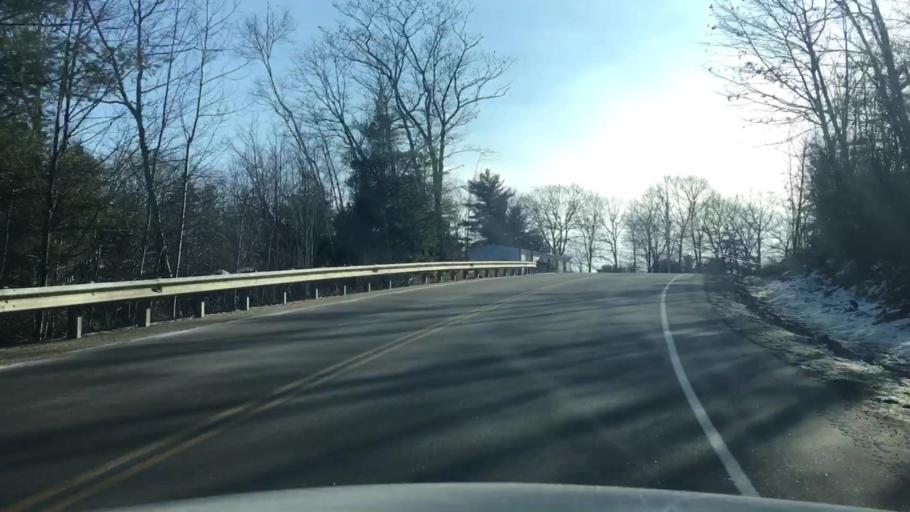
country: US
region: Maine
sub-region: Androscoggin County
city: Sabattus
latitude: 44.1159
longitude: -70.0867
